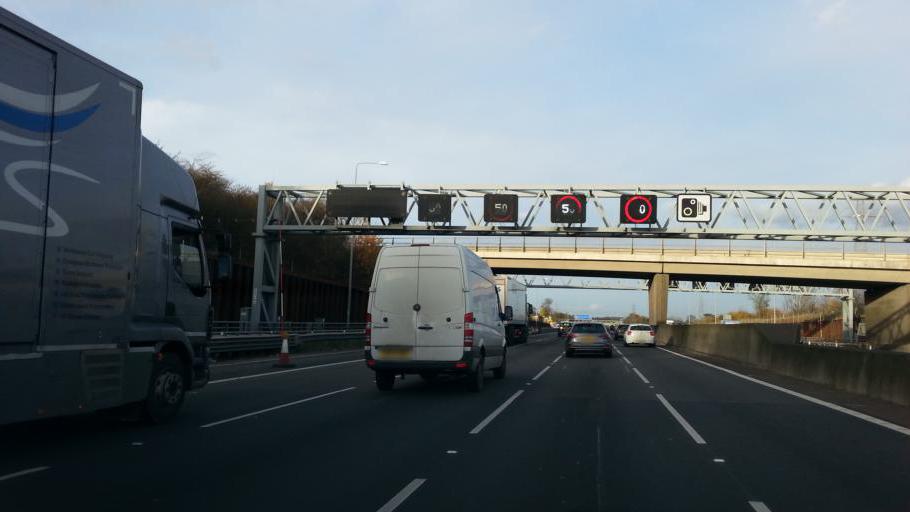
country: GB
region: England
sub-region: Buckinghamshire
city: Chalfont Saint Peter
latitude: 51.6132
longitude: -0.5271
